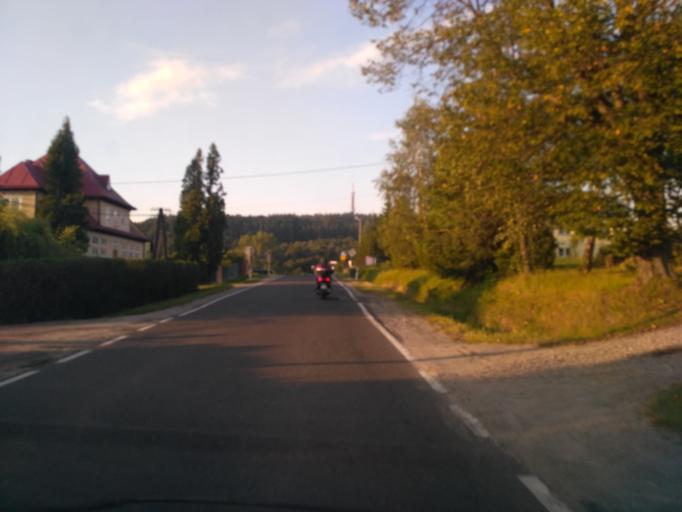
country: PL
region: Subcarpathian Voivodeship
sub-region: Powiat krosnienski
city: Korczyna
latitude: 49.7449
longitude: 21.8022
